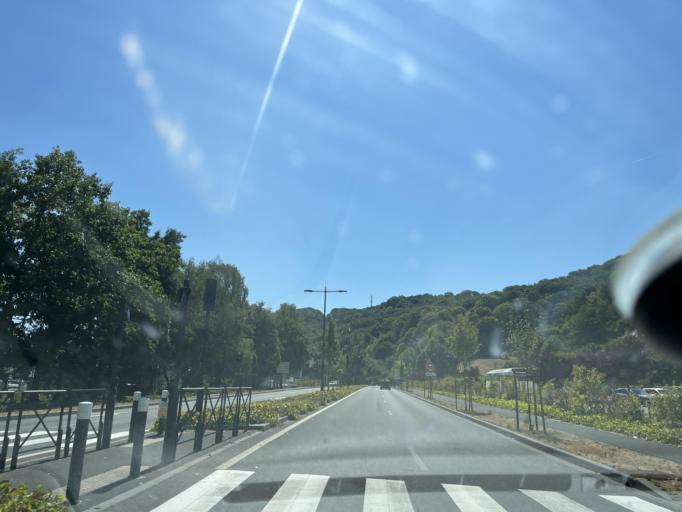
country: FR
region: Haute-Normandie
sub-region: Departement de la Seine-Maritime
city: Lillebonne
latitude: 49.5219
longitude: 0.5293
